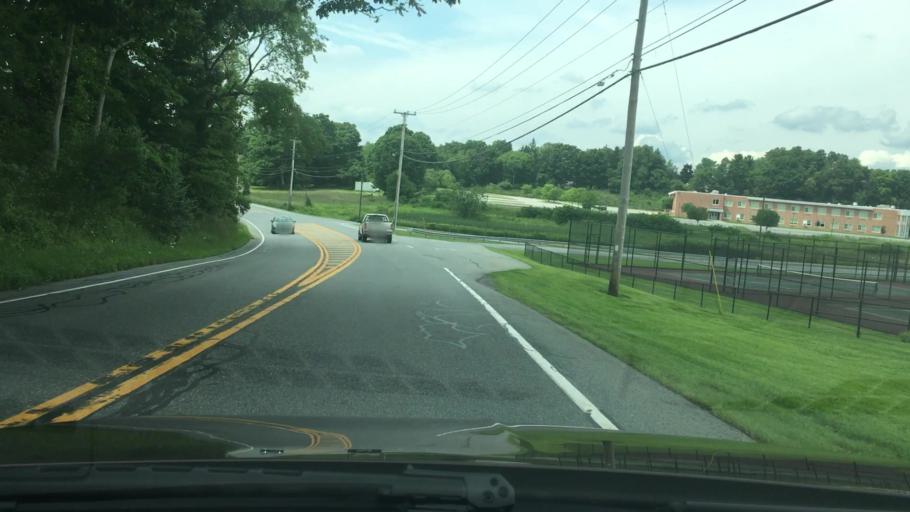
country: US
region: New York
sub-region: Dutchess County
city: Hillside Lake
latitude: 41.6511
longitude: -73.7349
